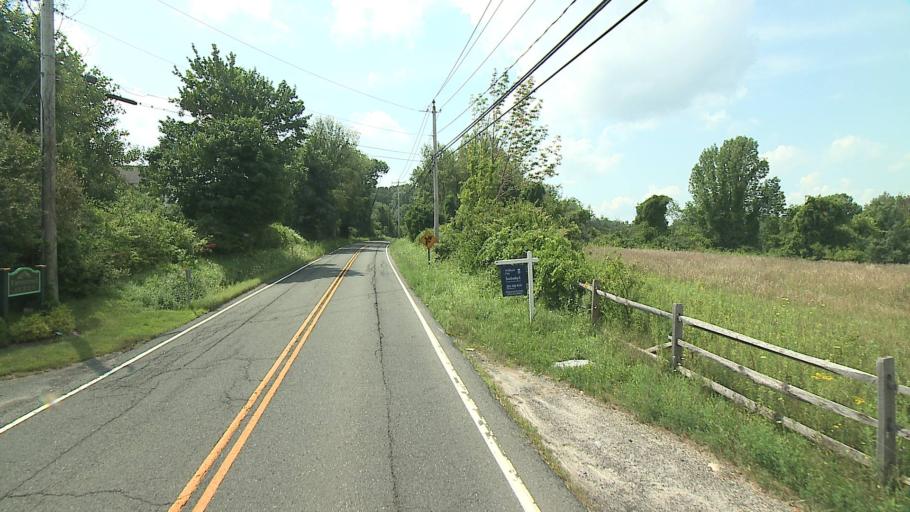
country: US
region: Connecticut
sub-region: Litchfield County
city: New Preston
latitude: 41.6226
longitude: -73.3730
